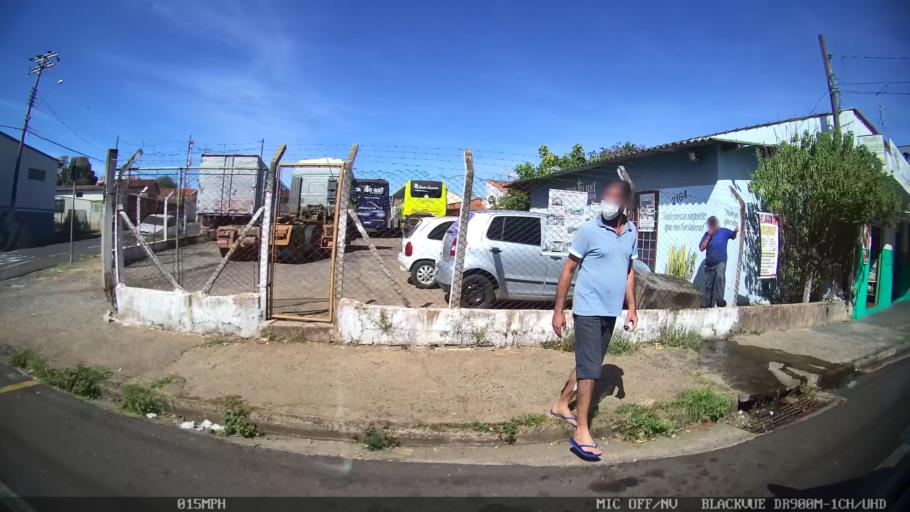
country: BR
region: Sao Paulo
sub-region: Franca
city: Franca
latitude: -20.5431
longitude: -47.3898
